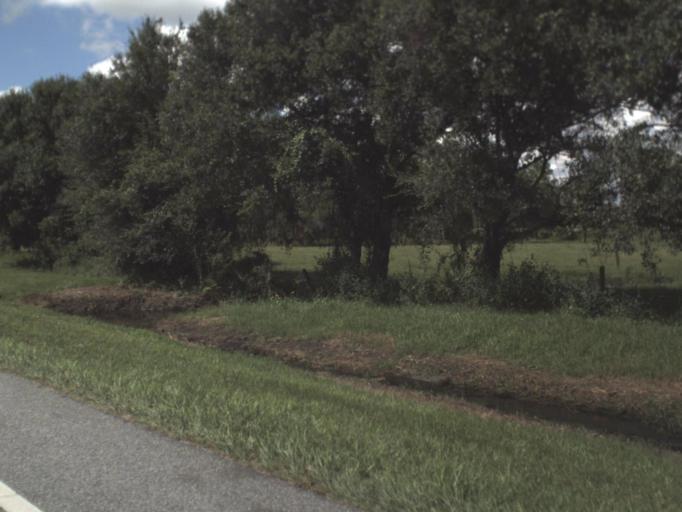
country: US
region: Florida
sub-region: Sarasota County
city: Lake Sarasota
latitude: 27.3368
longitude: -82.1389
